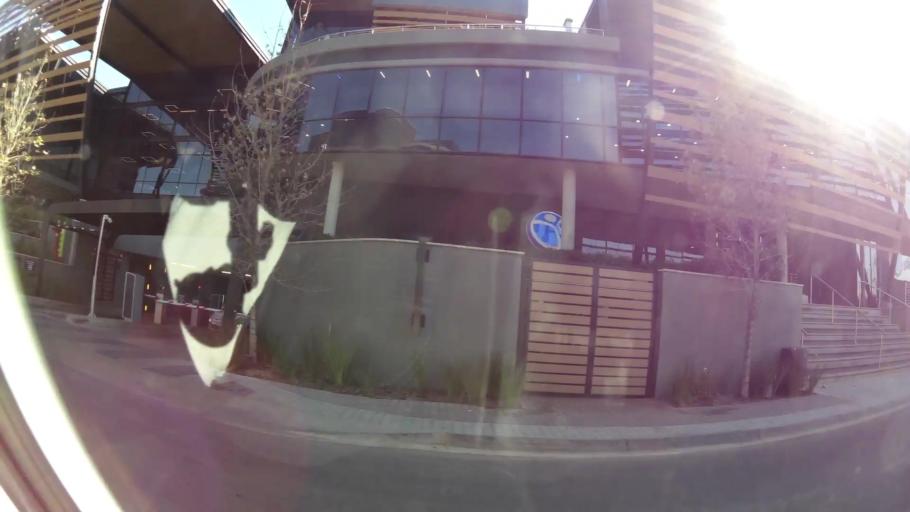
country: ZA
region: Gauteng
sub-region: City of Tshwane Metropolitan Municipality
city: Pretoria
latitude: -25.7775
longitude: 28.2570
